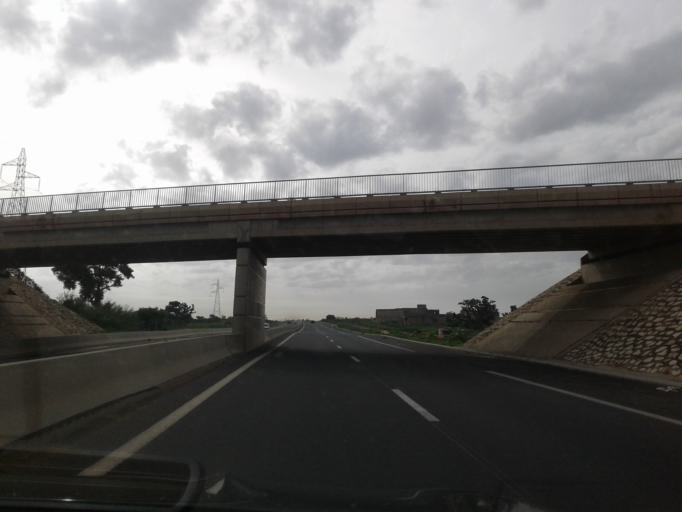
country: SN
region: Dakar
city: Pikine
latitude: 14.7357
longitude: -17.2538
